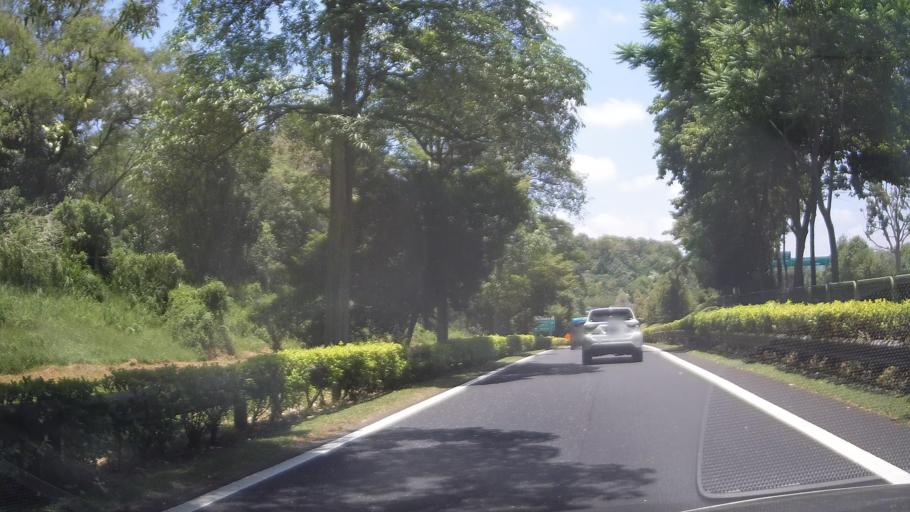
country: MY
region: Johor
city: Johor Bahru
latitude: 1.4076
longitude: 103.7719
